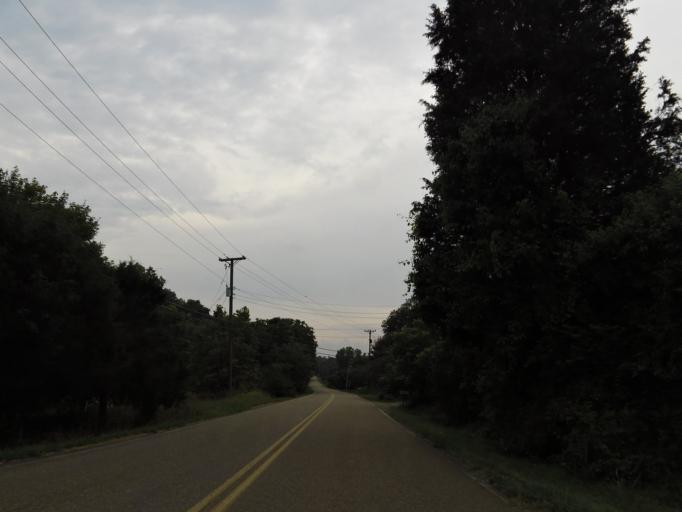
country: US
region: Tennessee
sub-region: Sevier County
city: Seymour
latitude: 35.9182
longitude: -83.8228
